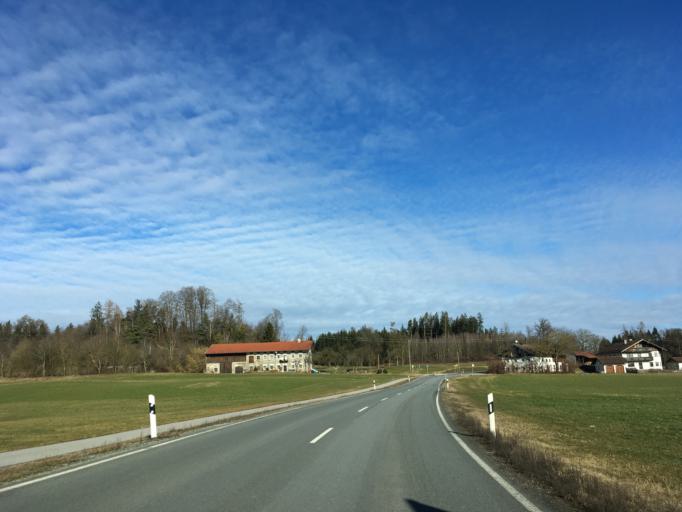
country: DE
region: Bavaria
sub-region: Upper Bavaria
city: Babensham
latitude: 48.0839
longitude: 12.2726
